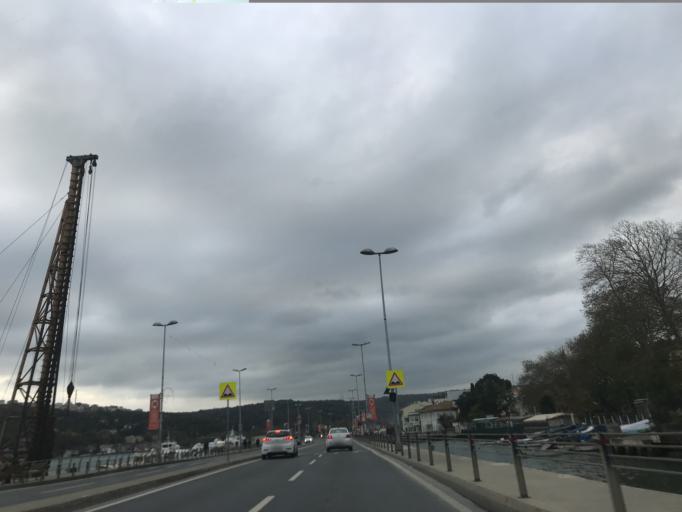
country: TR
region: Istanbul
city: Arikoey
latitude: 41.1608
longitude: 29.0456
